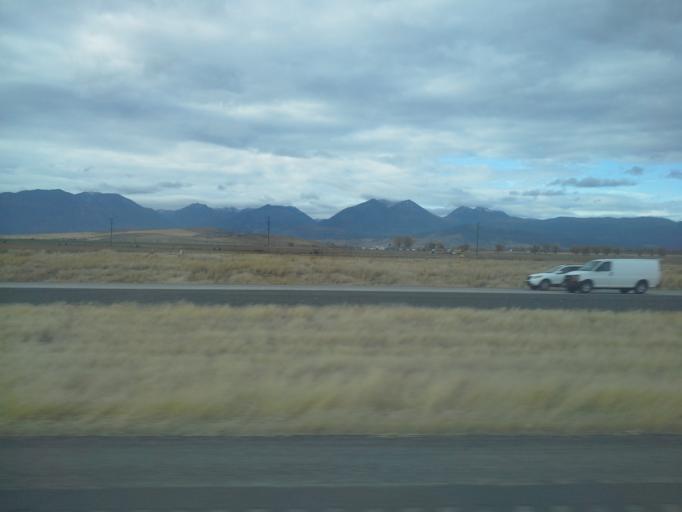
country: US
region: Oregon
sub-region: Union County
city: Union
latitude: 45.0050
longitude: -117.9088
